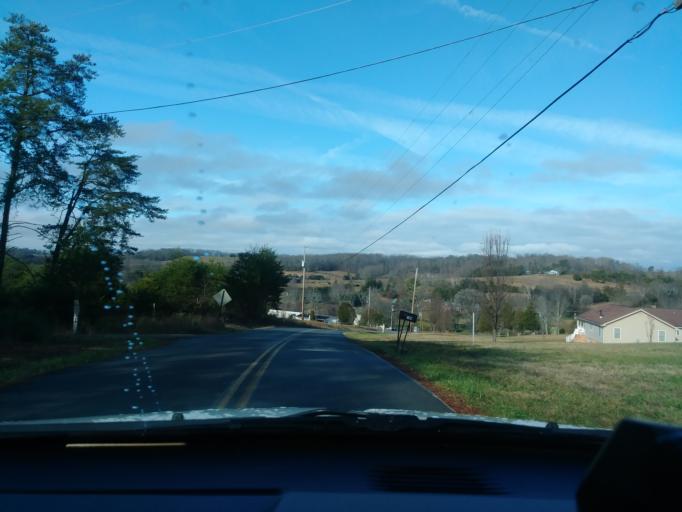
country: US
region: Tennessee
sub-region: Greene County
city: Mosheim
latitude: 36.0981
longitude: -82.9244
